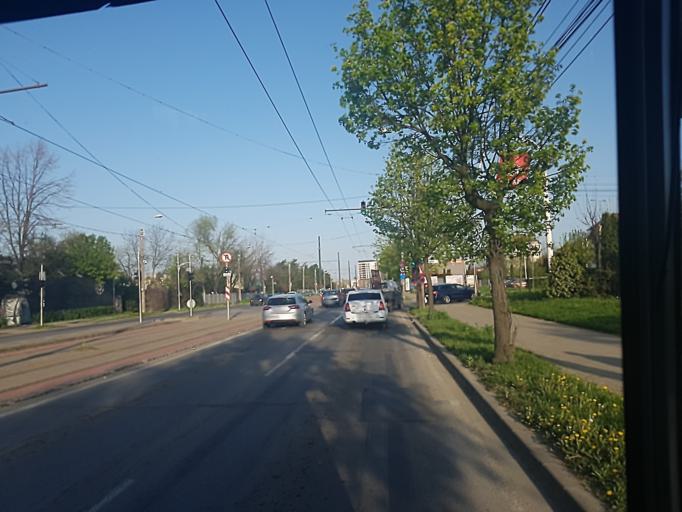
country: RO
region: Timis
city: Timisoara
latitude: 45.7378
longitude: 21.2440
